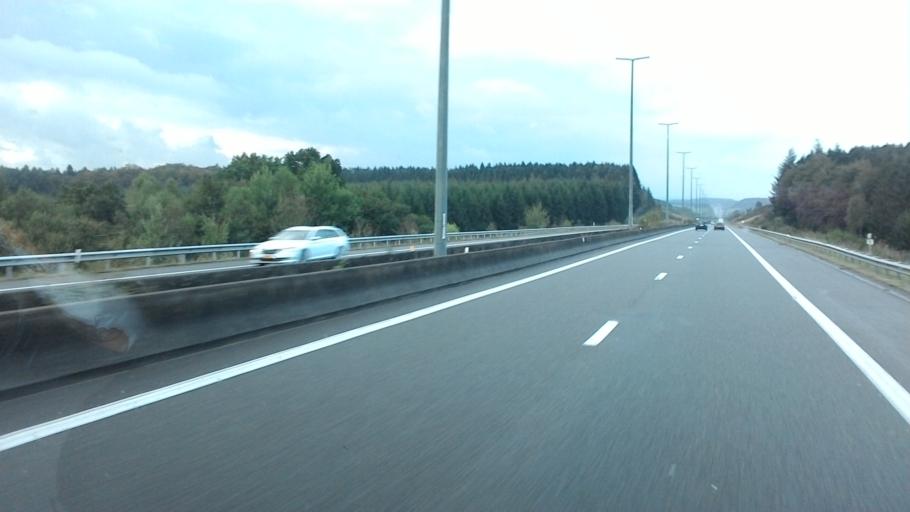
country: BE
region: Wallonia
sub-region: Province du Luxembourg
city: Bastogne
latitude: 50.0624
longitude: 5.7276
